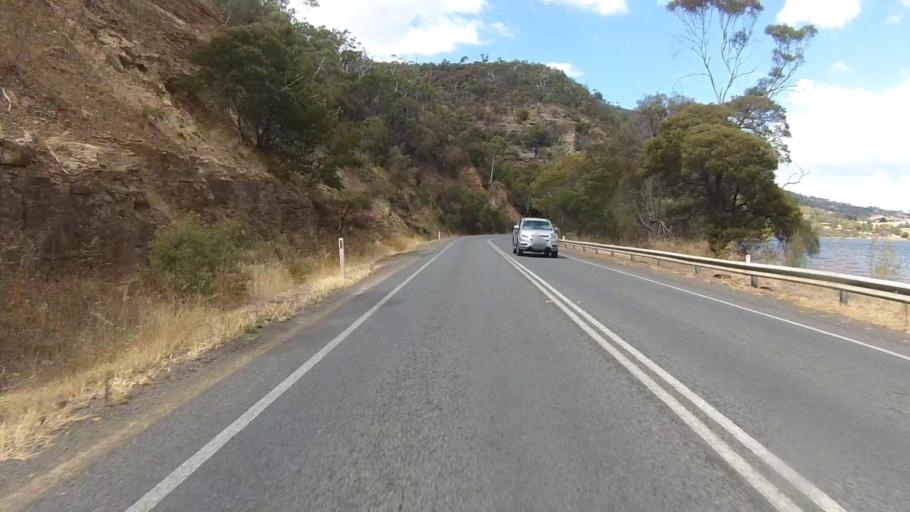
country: AU
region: Tasmania
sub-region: Brighton
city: Old Beach
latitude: -42.7853
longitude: 147.2899
